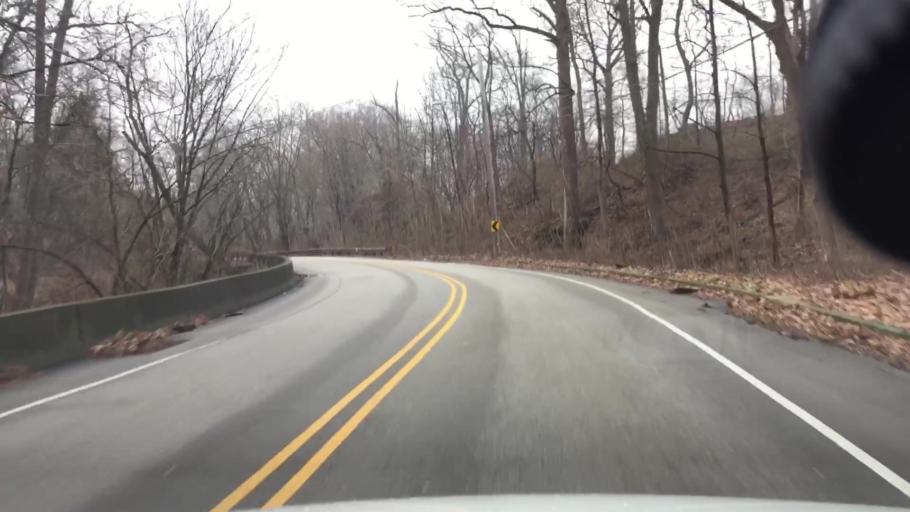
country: US
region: Pennsylvania
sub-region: Montgomery County
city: Wyndmoor
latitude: 40.0644
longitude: -75.1991
